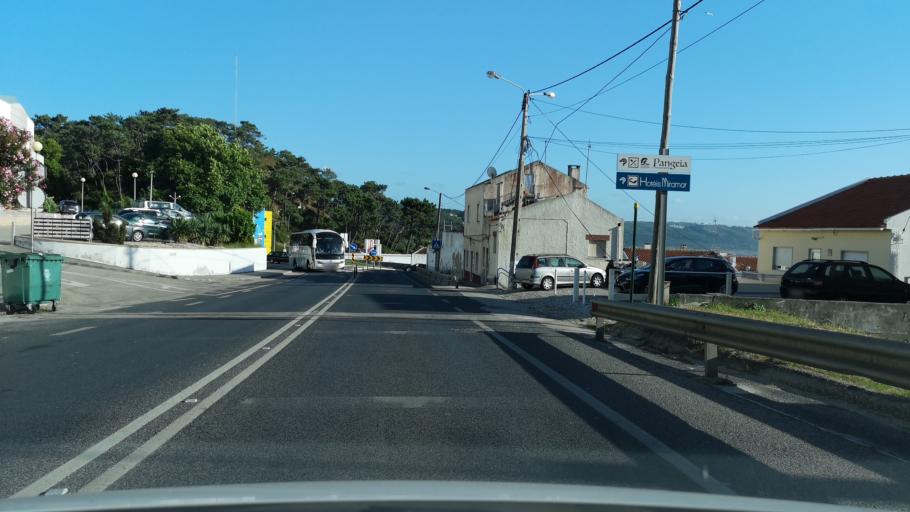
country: PT
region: Leiria
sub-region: Nazare
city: Nazare
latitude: 39.6023
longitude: -9.0678
